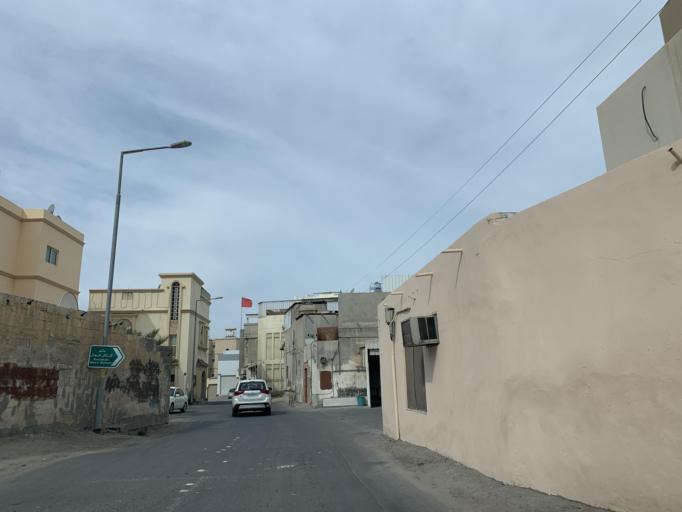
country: BH
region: Central Governorate
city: Madinat Hamad
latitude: 26.1137
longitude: 50.4808
